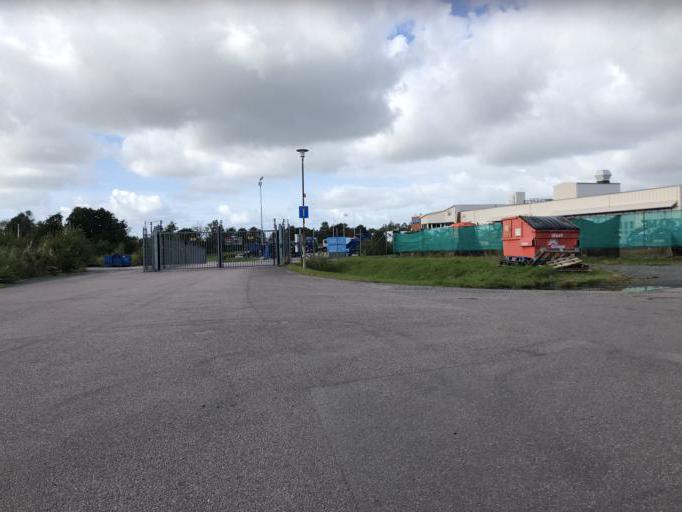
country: SE
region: Vaestra Goetaland
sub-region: Goteborg
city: Majorna
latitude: 57.7505
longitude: 11.8786
